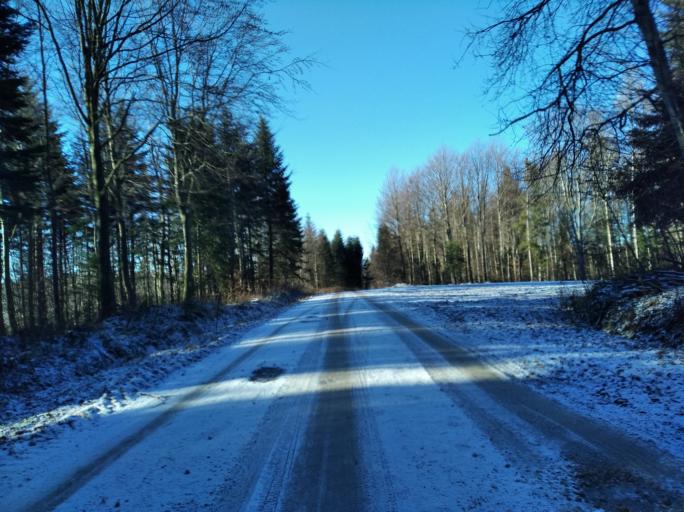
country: PL
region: Subcarpathian Voivodeship
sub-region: Powiat strzyzowski
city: Czudec
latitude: 49.9724
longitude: 21.7969
